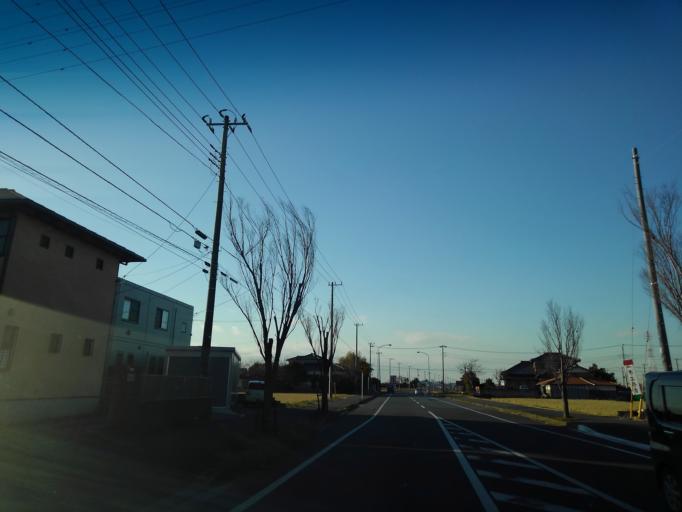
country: JP
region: Chiba
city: Kimitsu
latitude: 35.3125
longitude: 139.9169
